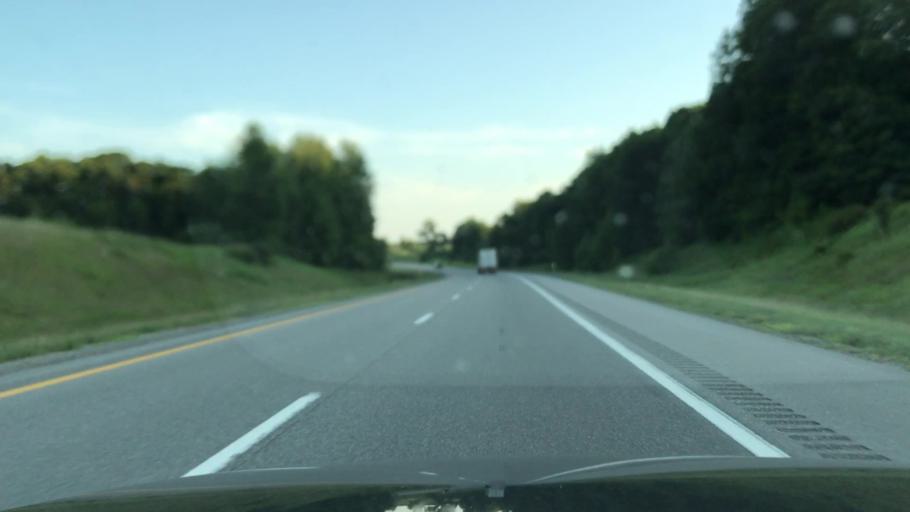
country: US
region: Michigan
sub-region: Osceola County
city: Reed City
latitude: 43.8676
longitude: -85.5341
